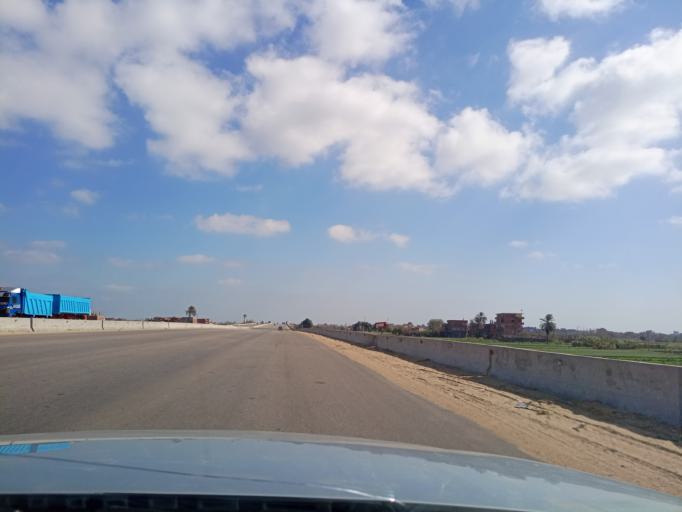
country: EG
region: Muhafazat al Minufiyah
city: Al Bajur
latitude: 30.3990
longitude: 31.0203
